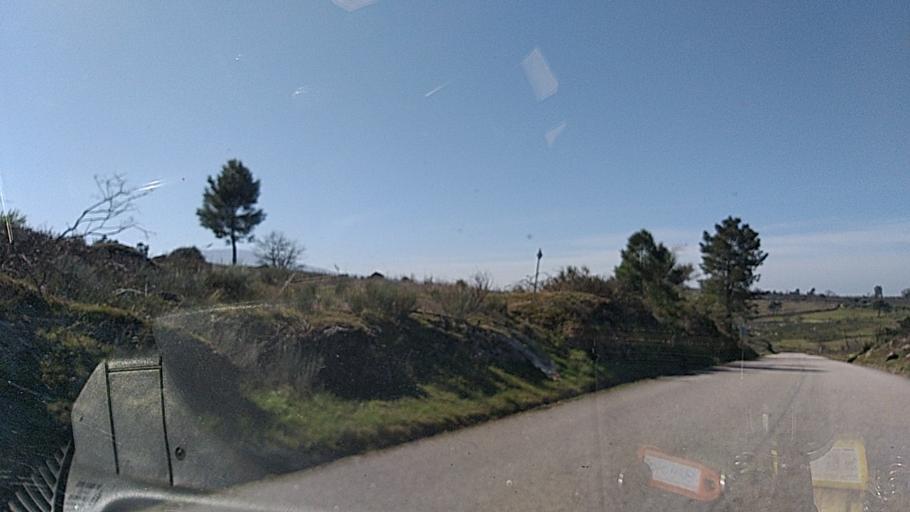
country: PT
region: Guarda
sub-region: Celorico da Beira
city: Celorico da Beira
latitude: 40.5923
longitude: -7.4526
